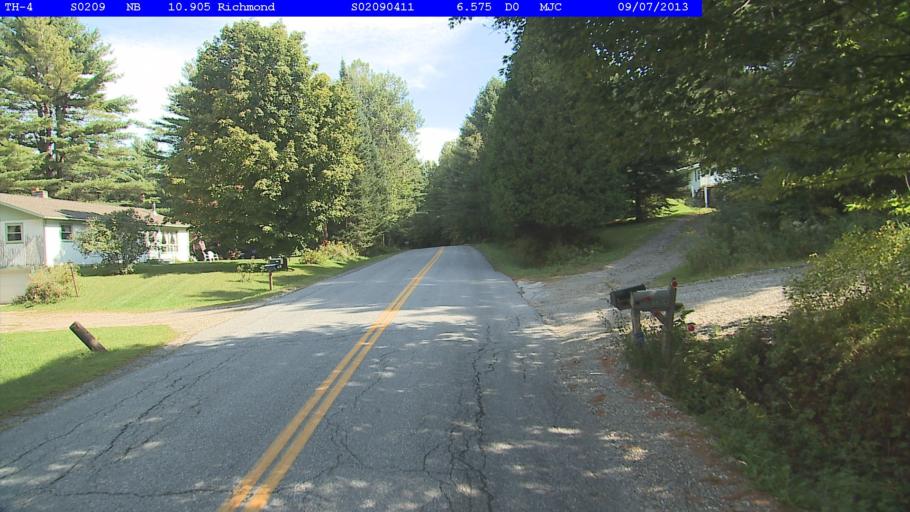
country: US
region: Vermont
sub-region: Chittenden County
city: Jericho
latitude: 44.4195
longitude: -72.9795
